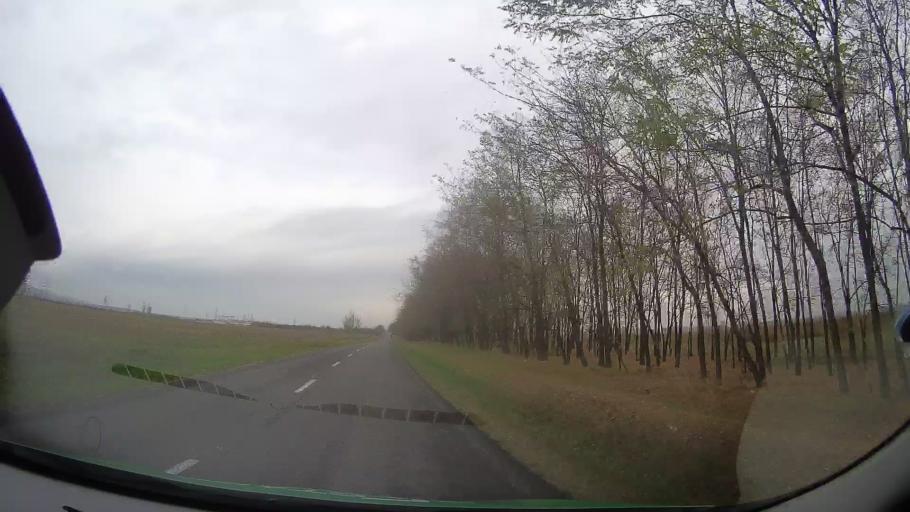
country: RO
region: Prahova
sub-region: Comuna Berceni
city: Berceni
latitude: 44.9399
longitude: 26.1067
